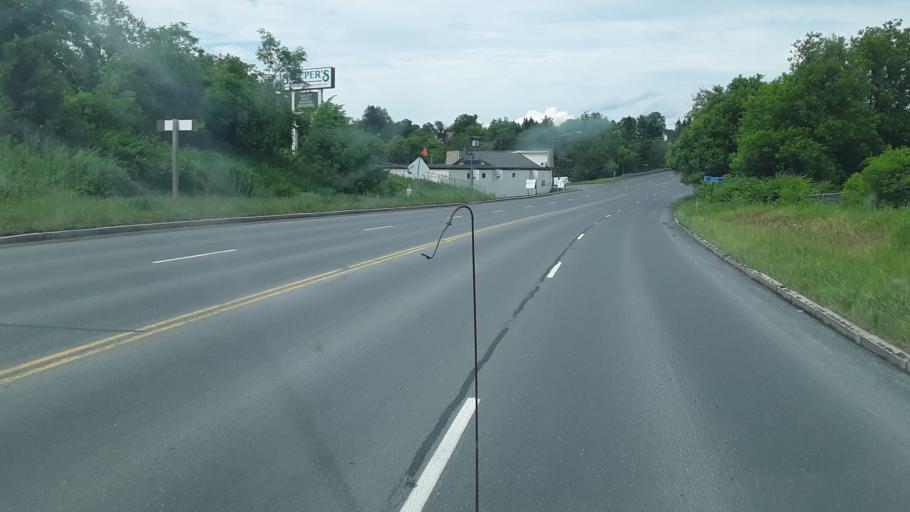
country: US
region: Maine
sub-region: Aroostook County
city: Caribou
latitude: 46.8555
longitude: -68.0061
